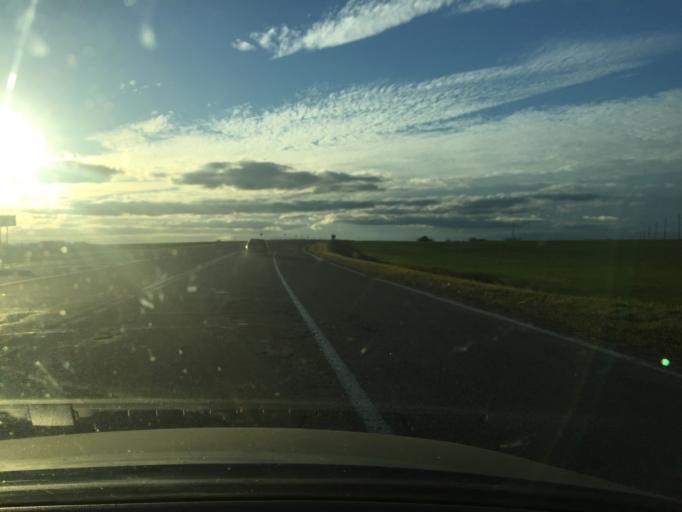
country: BY
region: Vitebsk
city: Vyerkhnyadzvinsk
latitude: 55.8370
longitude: 27.9093
